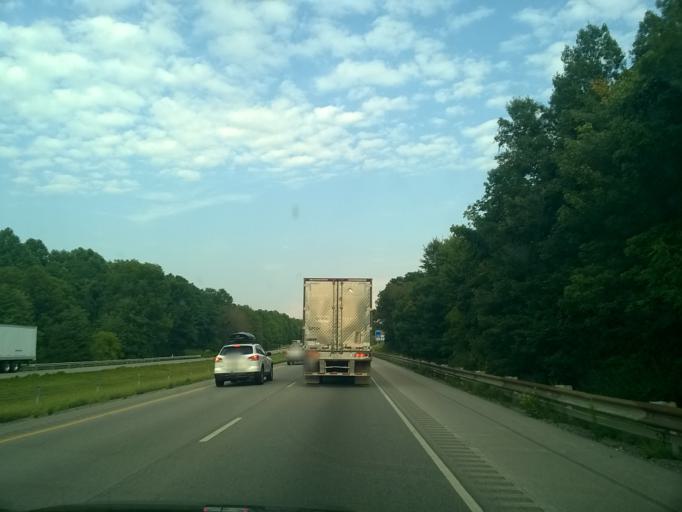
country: US
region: Indiana
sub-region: Putnam County
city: Cloverdale
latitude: 39.5329
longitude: -86.8424
